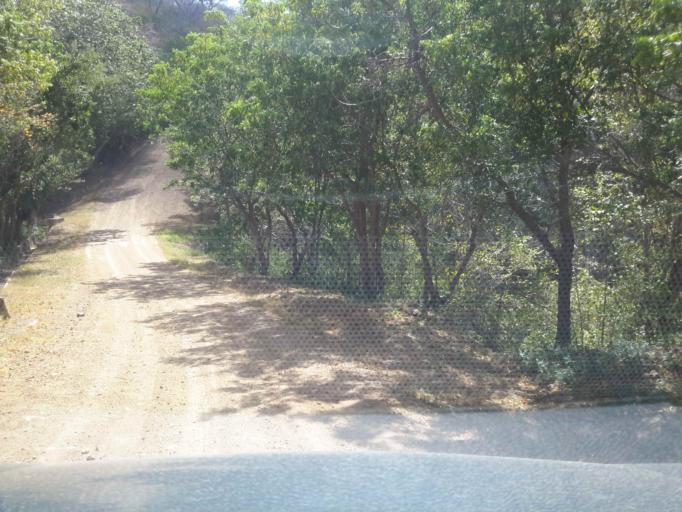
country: NI
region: Rivas
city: San Juan del Sur
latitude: 11.1843
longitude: -85.8123
